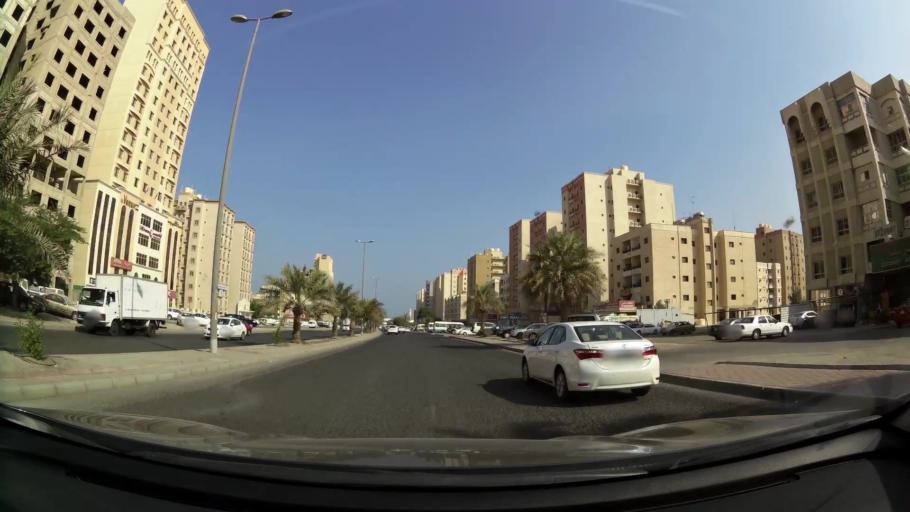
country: KW
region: Al Ahmadi
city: Al Mahbulah
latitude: 29.1373
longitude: 48.1232
